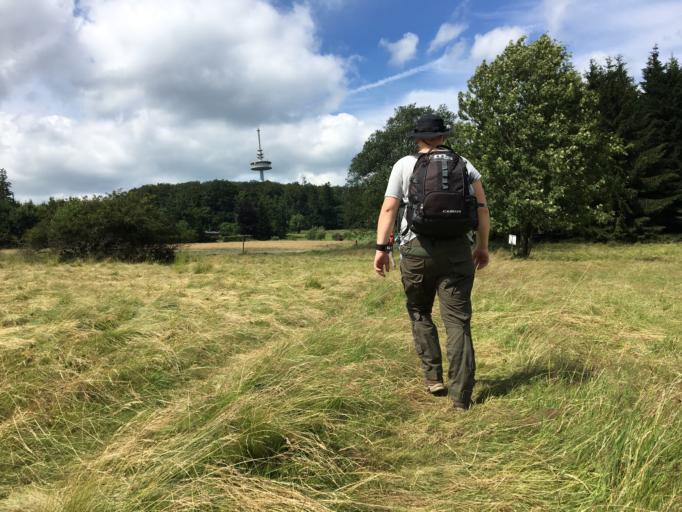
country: DE
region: Hesse
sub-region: Regierungsbezirk Giessen
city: Ulrichstein
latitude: 50.5030
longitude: 9.2285
